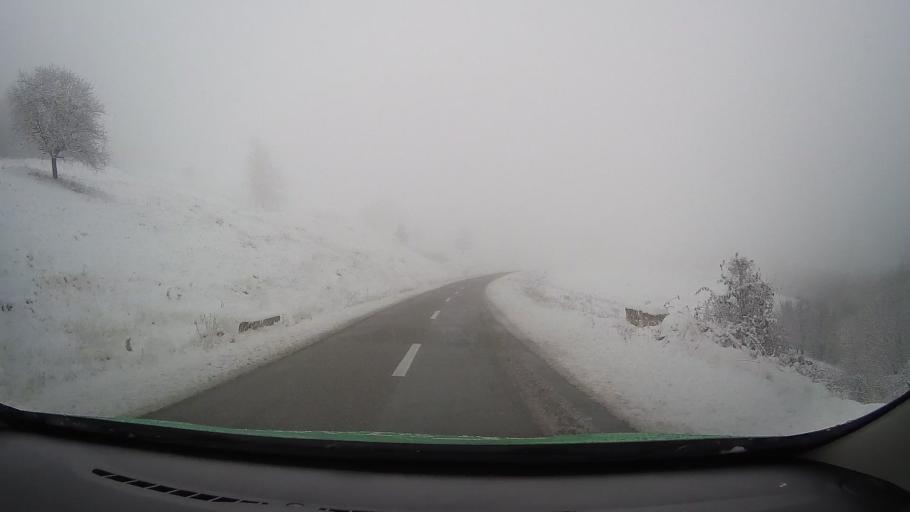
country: RO
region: Hunedoara
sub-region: Comuna Teliucu Inferior
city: Teliucu Inferior
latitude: 45.6679
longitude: 22.9179
